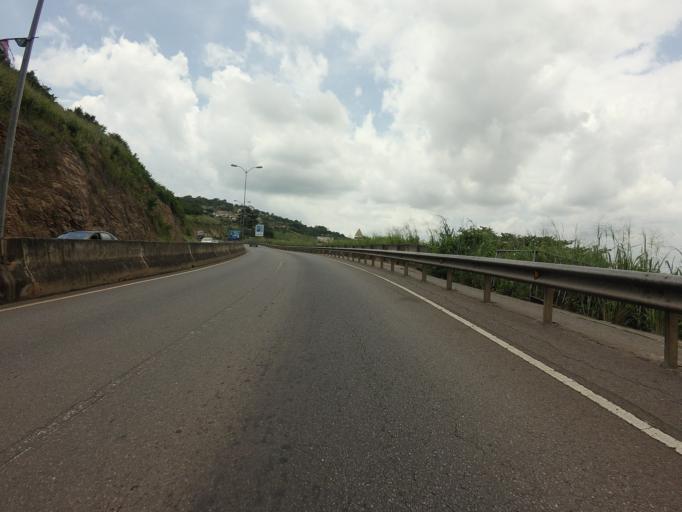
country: GH
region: Eastern
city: Aburi
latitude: 5.7896
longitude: -0.1879
